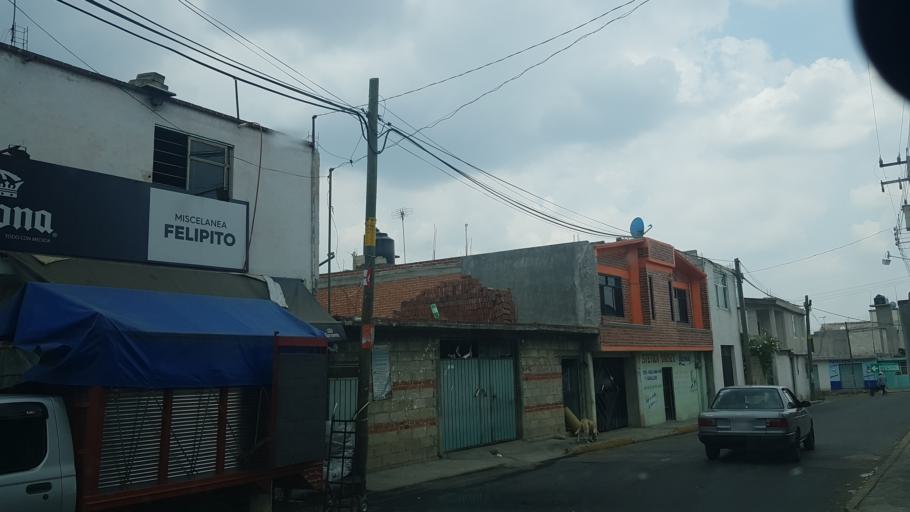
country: MX
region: Puebla
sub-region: Huejotzingo
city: San Miguel Tianguizolco
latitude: 19.1593
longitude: -98.4418
